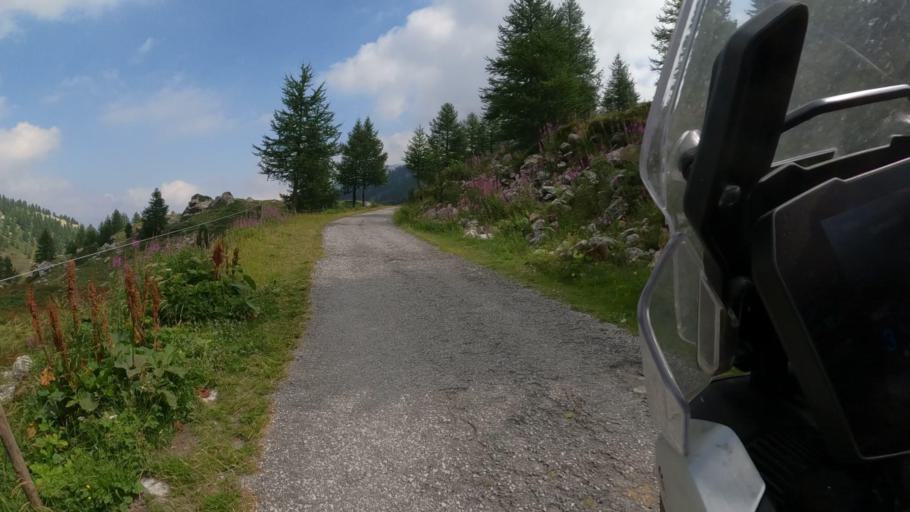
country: IT
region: Piedmont
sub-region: Provincia di Cuneo
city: Marmora
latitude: 44.3982
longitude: 7.1081
